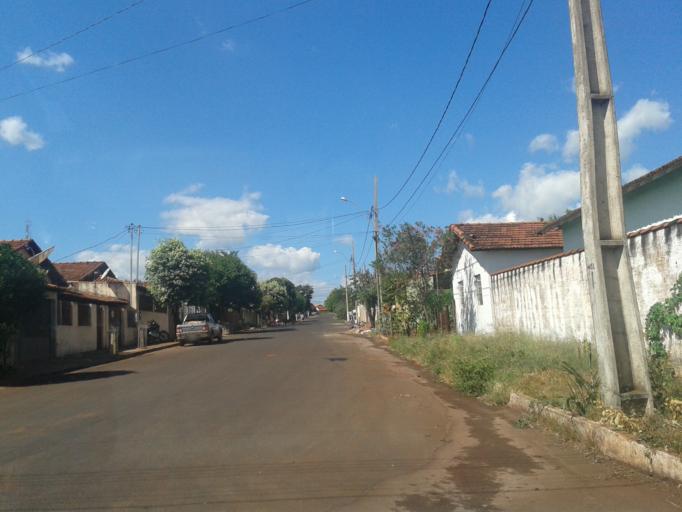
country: BR
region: Minas Gerais
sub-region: Capinopolis
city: Capinopolis
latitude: -18.6932
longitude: -49.5684
